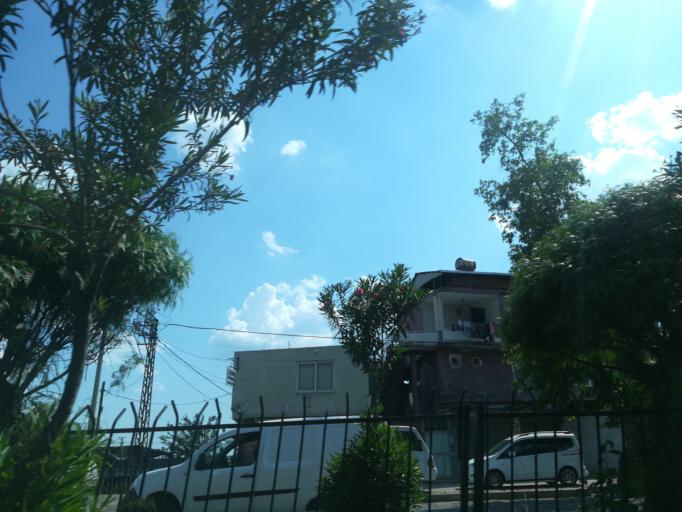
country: TR
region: Adana
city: Yuregir
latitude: 36.9887
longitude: 35.3454
